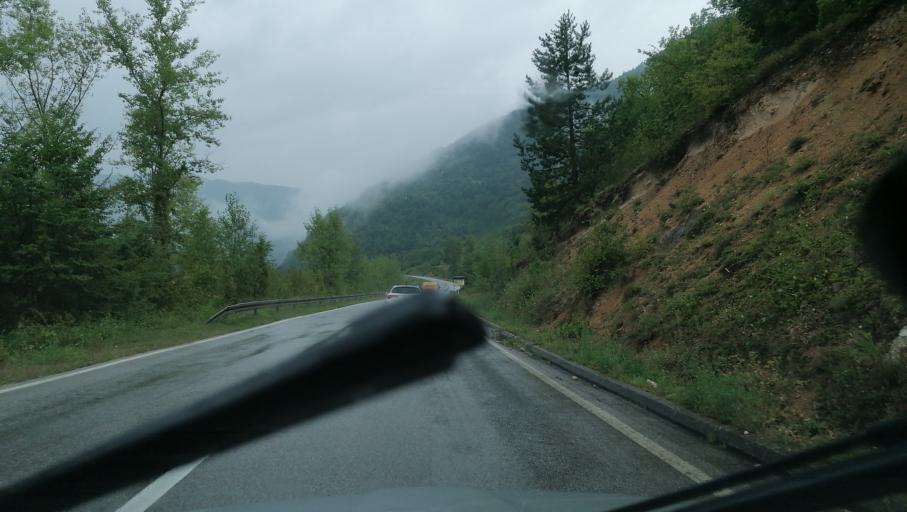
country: BA
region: Republika Srpska
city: Visegrad
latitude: 43.7190
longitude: 19.1687
